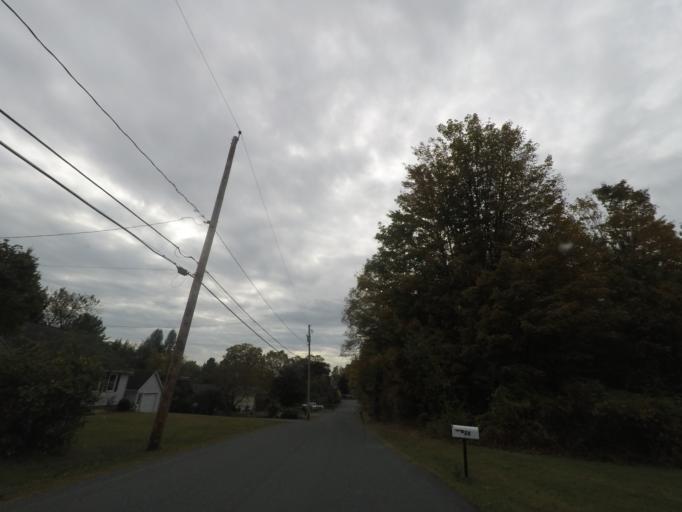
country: US
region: New York
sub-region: Rensselaer County
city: Nassau
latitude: 42.5393
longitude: -73.6608
